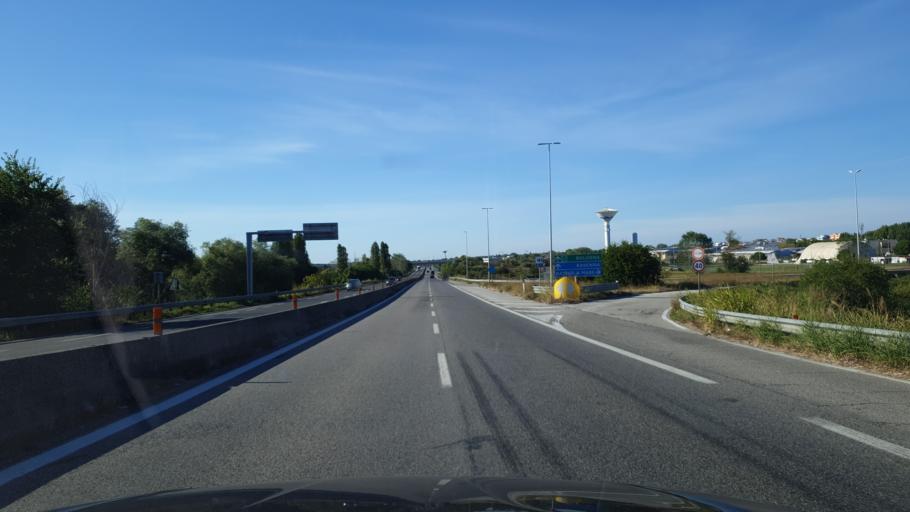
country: IT
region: Emilia-Romagna
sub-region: Forli-Cesena
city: Gatteo a Mare
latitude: 44.1689
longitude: 12.4233
